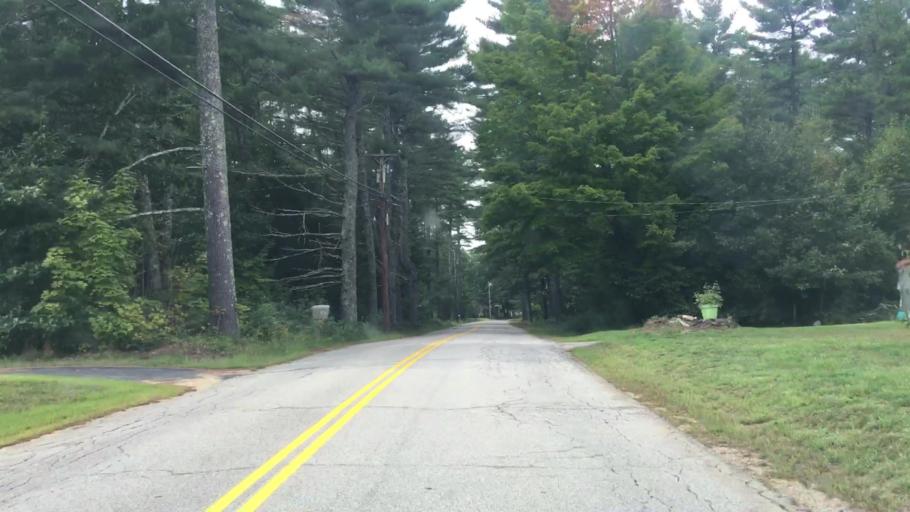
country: US
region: New Hampshire
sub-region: Strafford County
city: Barrington
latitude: 43.2013
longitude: -71.0005
